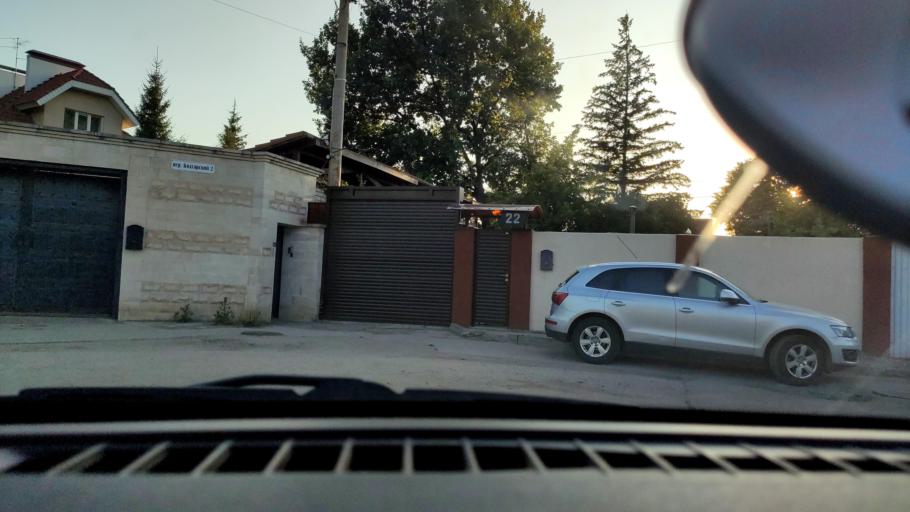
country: RU
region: Samara
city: Samara
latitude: 53.2610
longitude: 50.1911
